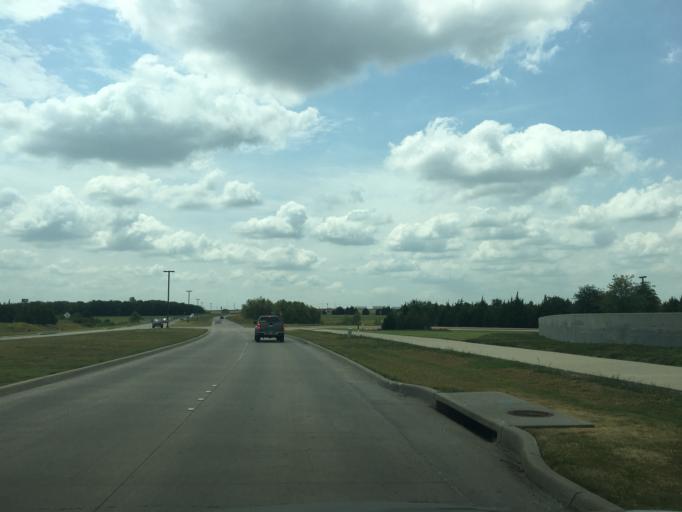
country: US
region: Texas
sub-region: Rockwall County
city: Rockwall
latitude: 32.9226
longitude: -96.4356
